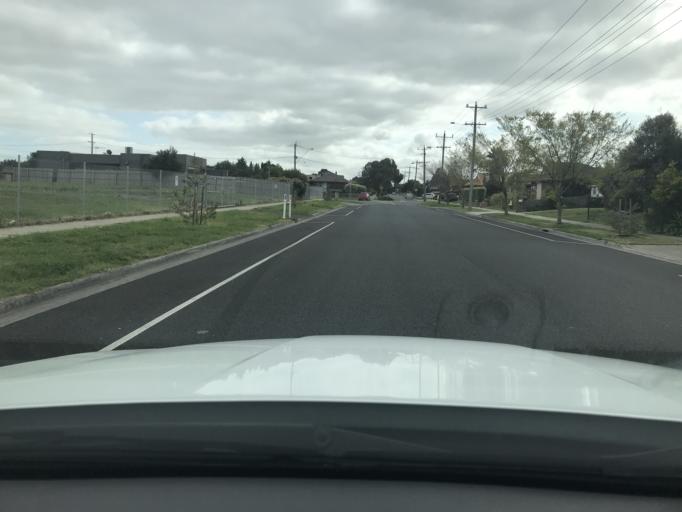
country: AU
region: Victoria
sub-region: Hume
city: Craigieburn
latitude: -37.5962
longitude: 144.9220
